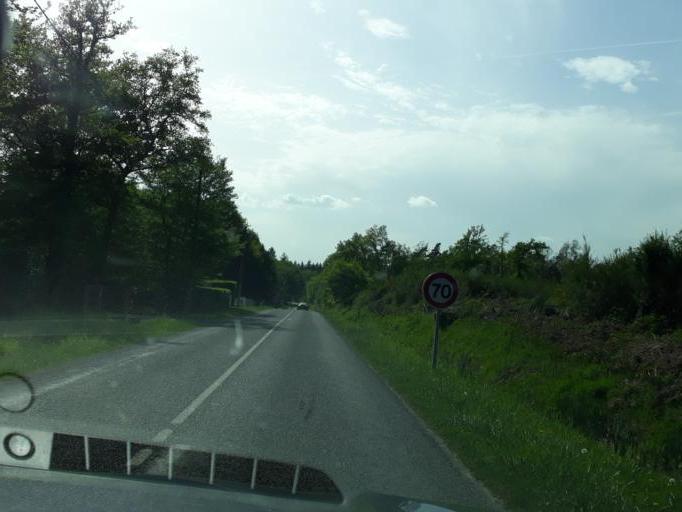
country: FR
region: Centre
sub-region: Departement du Loir-et-Cher
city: Dhuizon
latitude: 47.6596
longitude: 1.6669
